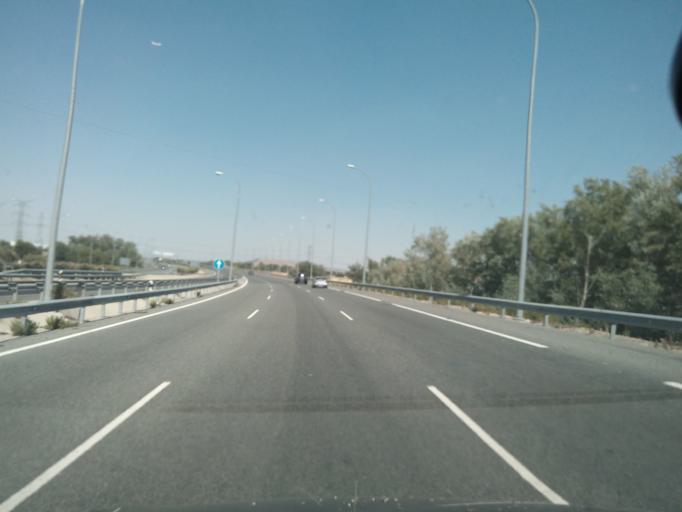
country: ES
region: Madrid
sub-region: Provincia de Madrid
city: San Fernando de Henares
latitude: 40.4117
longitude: -3.5091
